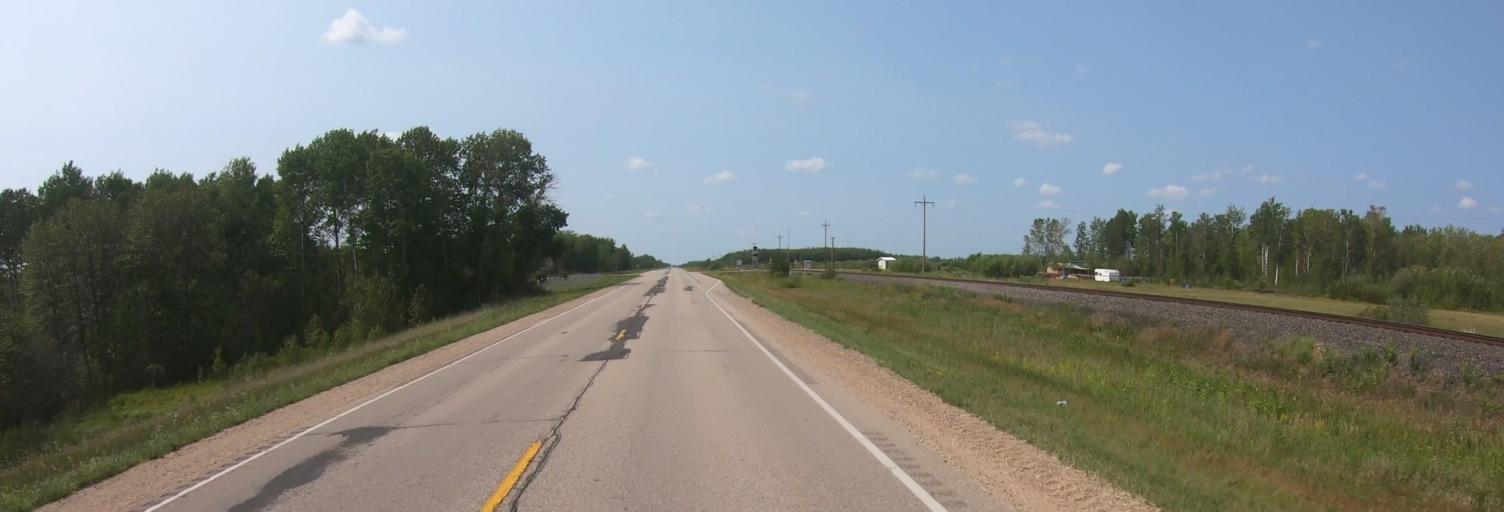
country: US
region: Minnesota
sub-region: Lake of the Woods County
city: Baudette
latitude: 48.7476
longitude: -94.8692
